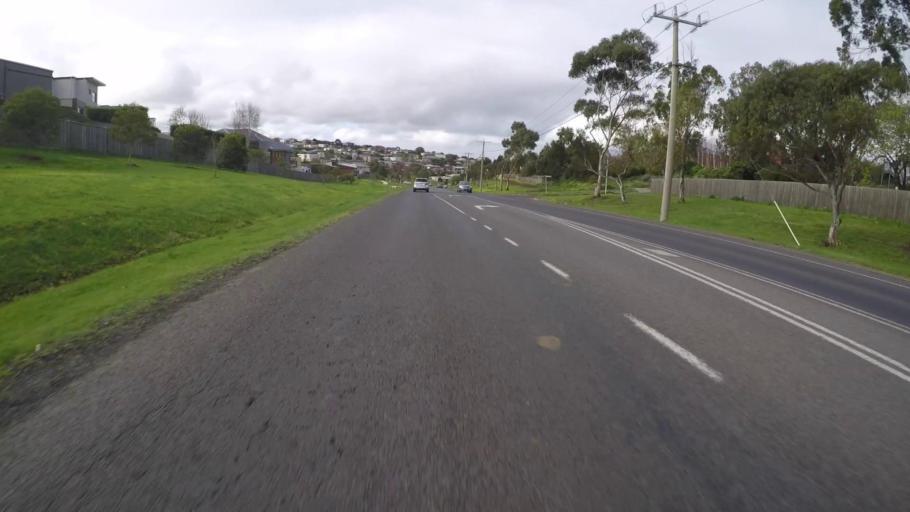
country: AU
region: Victoria
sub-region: Greater Geelong
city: Wandana Heights
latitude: -38.1698
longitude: 144.3026
